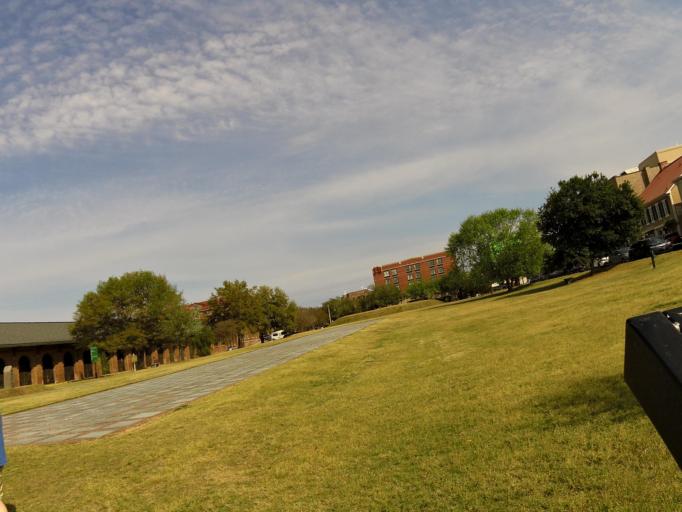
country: US
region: Florida
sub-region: Franklin County
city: Carrabelle
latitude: 29.3303
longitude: -84.3892
